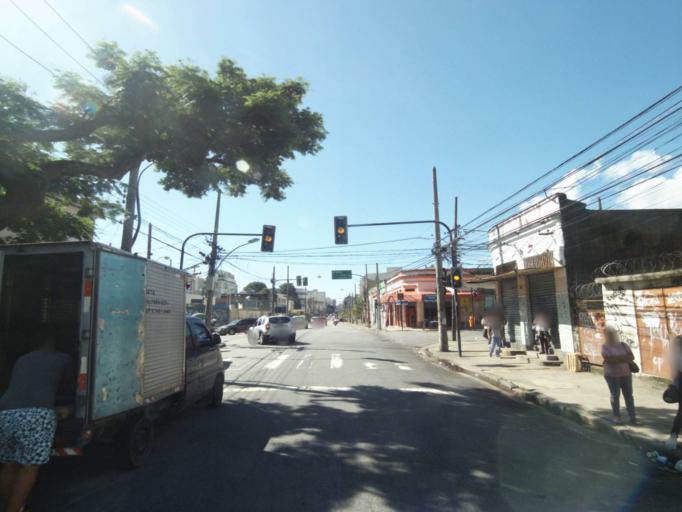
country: BR
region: Rio de Janeiro
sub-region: Rio De Janeiro
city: Rio de Janeiro
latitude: -22.9115
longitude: -43.2857
